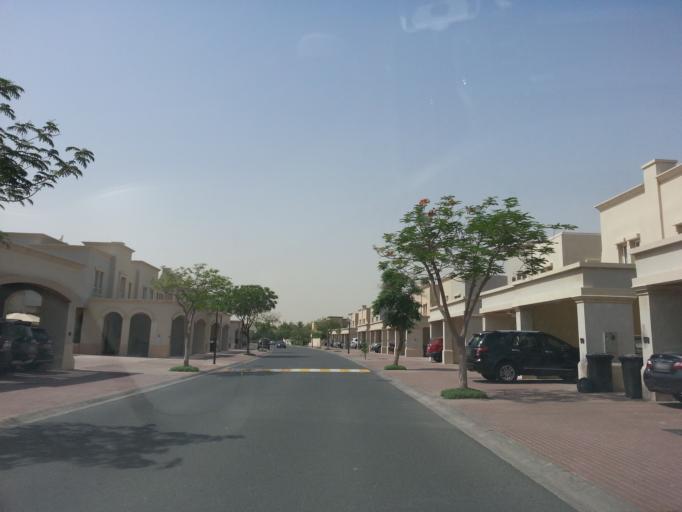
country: AE
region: Dubai
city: Dubai
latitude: 25.0523
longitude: 55.1735
